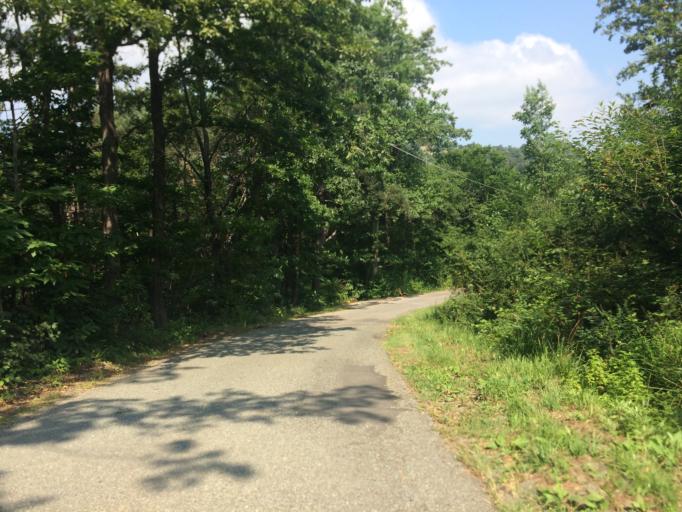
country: IT
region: Liguria
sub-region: Provincia di Savona
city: Molino-Pera
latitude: 44.4868
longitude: 8.3492
